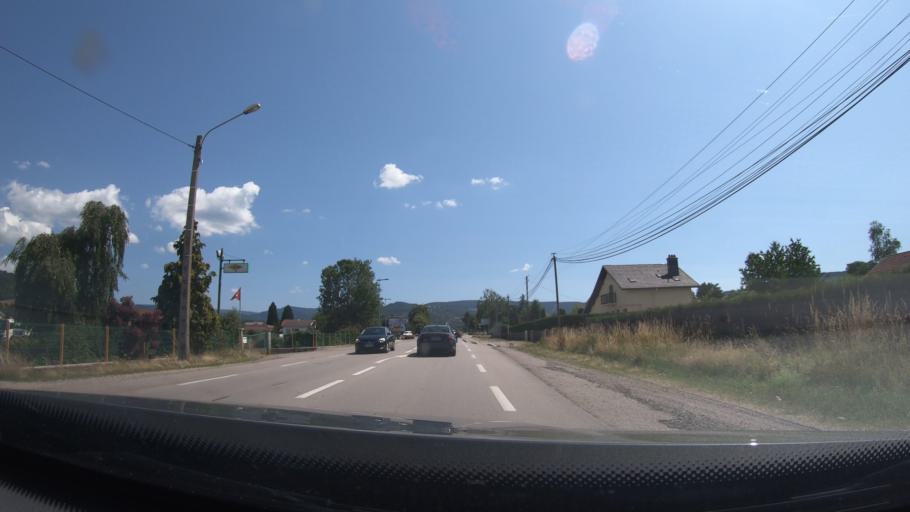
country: FR
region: Lorraine
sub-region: Departement des Vosges
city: Saint-Leonard
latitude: 48.2079
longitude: 6.9436
